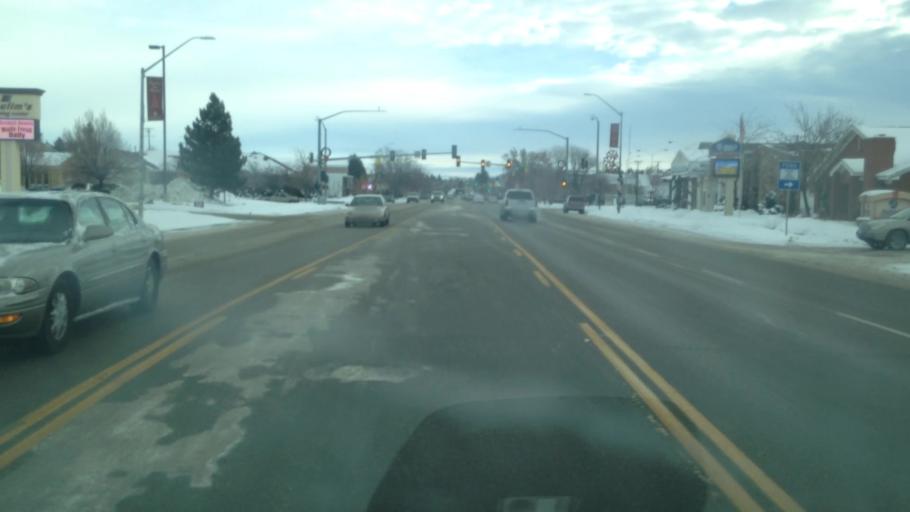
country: US
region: Idaho
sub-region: Madison County
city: Rexburg
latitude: 43.8261
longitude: -111.7884
